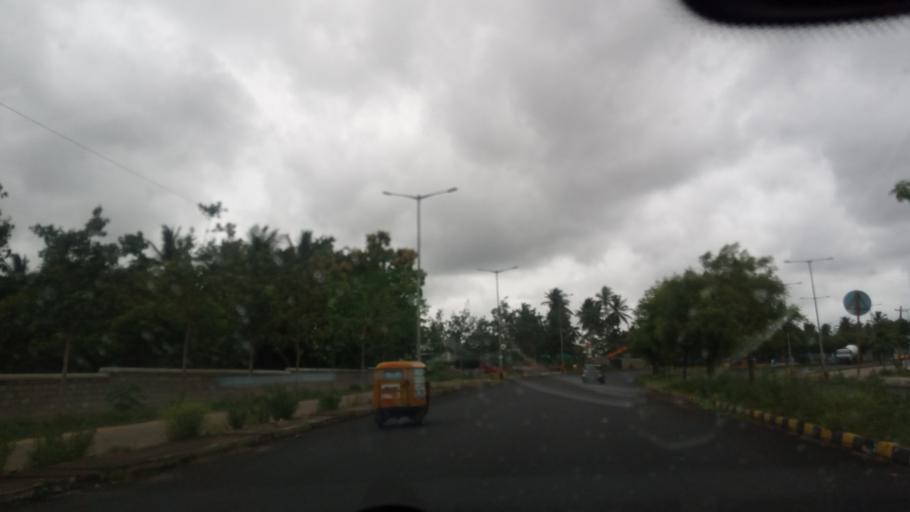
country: IN
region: Karnataka
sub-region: Mysore
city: Mysore
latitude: 12.3077
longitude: 76.6000
